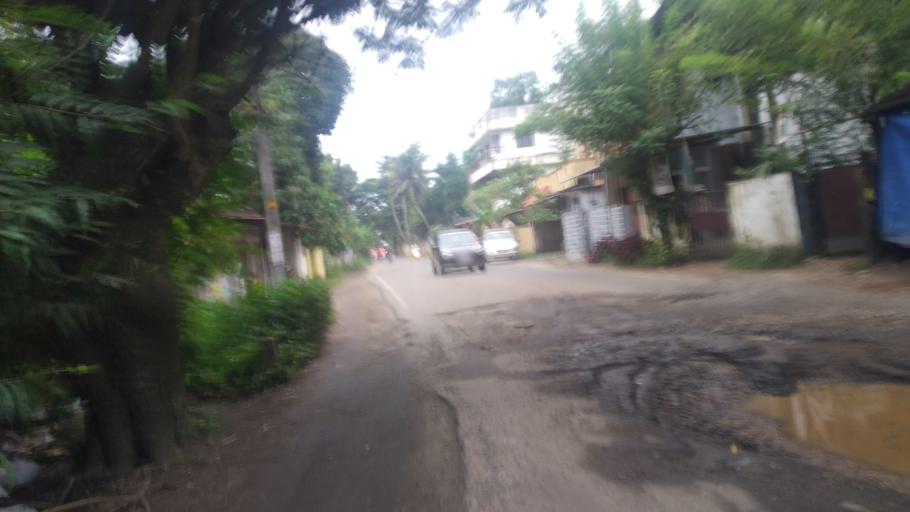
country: IN
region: Kerala
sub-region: Alappuzha
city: Arukutti
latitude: 9.8687
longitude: 76.2910
